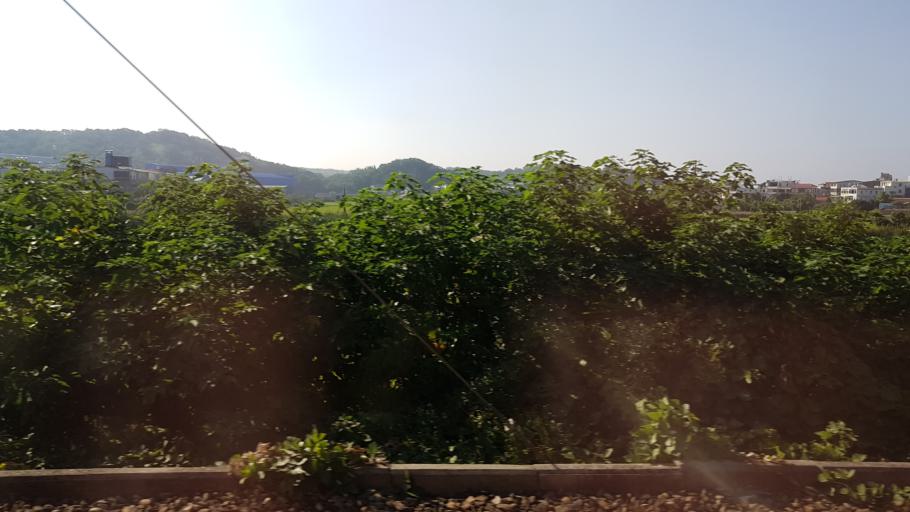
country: TW
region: Taiwan
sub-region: Miaoli
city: Miaoli
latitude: 24.6509
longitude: 120.8762
